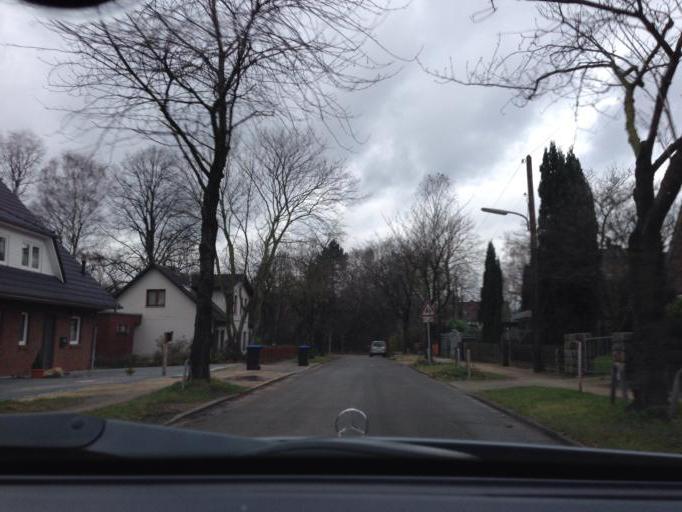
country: DE
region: Hamburg
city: Farmsen-Berne
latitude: 53.5867
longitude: 10.1142
